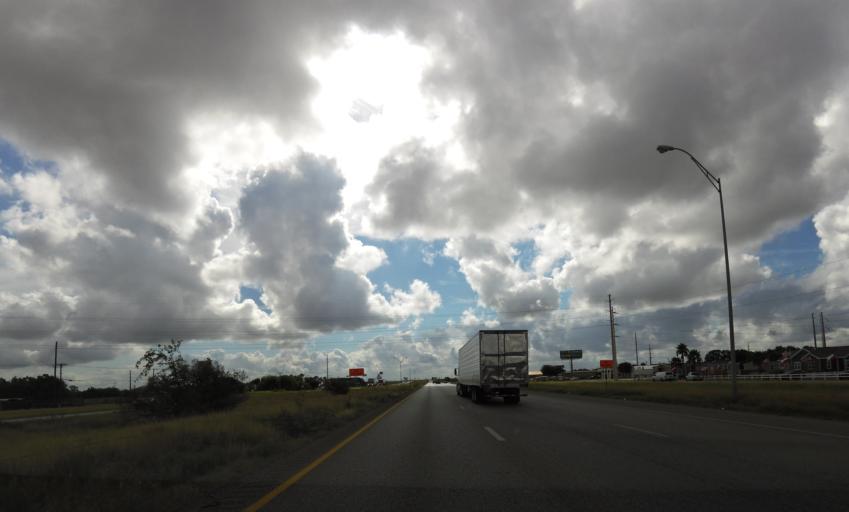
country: US
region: Texas
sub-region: Guadalupe County
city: Seguin
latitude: 29.5992
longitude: -97.9594
